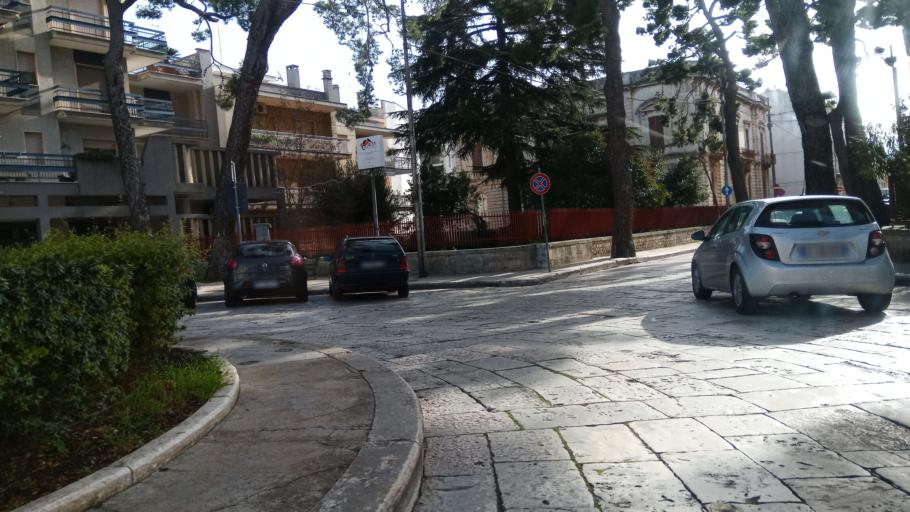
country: IT
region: Apulia
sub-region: Provincia di Bari
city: Castellana
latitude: 40.8869
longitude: 17.1665
